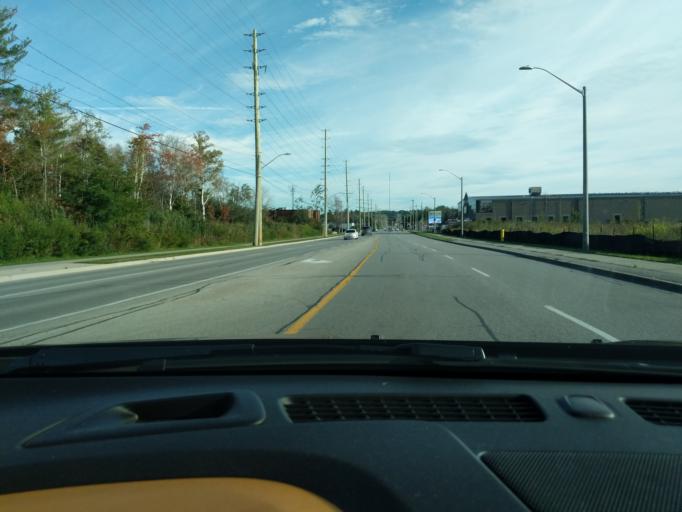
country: CA
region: Ontario
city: Barrie
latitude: 44.3789
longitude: -79.7226
